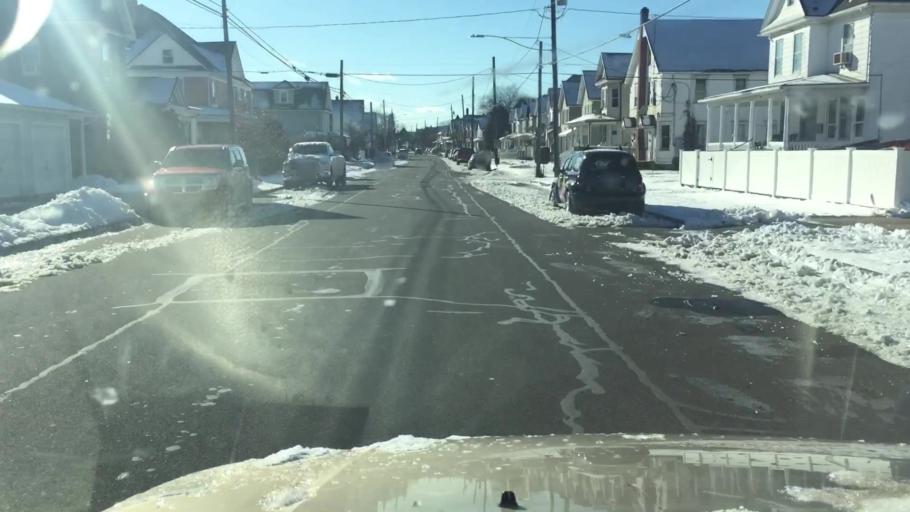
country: US
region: Pennsylvania
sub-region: Luzerne County
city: East Berwick
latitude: 41.0588
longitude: -76.2267
